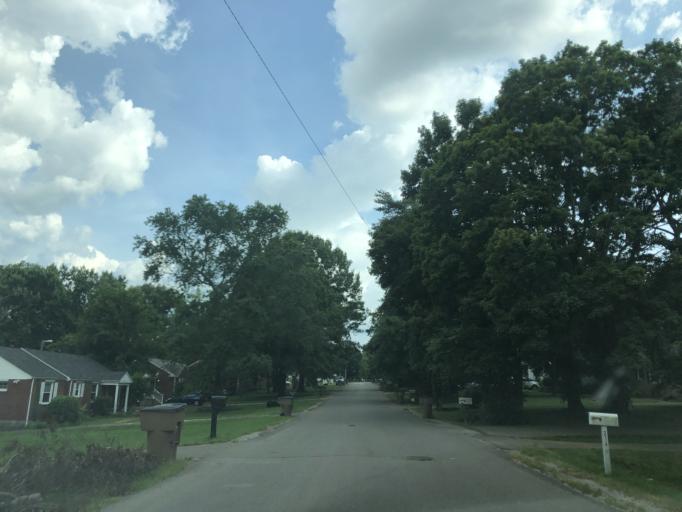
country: US
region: Tennessee
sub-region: Davidson County
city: Lakewood
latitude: 36.1664
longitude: -86.6788
